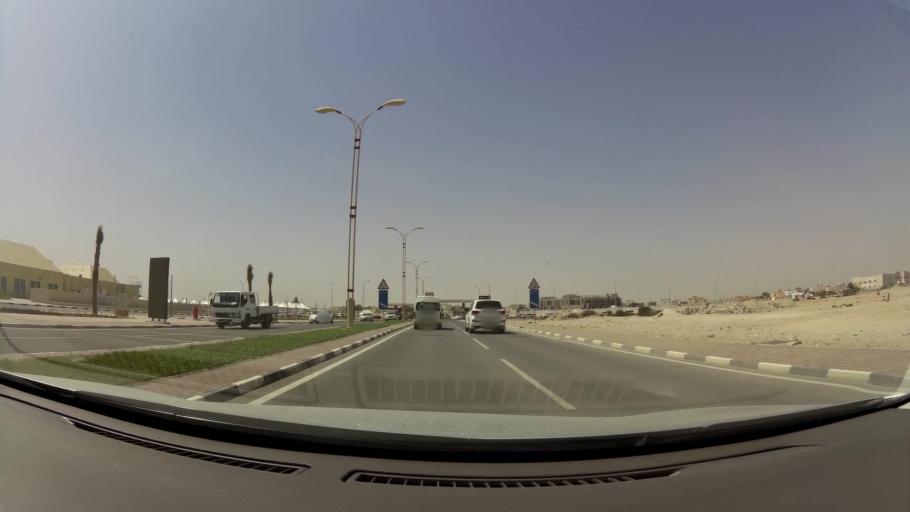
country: QA
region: Baladiyat Umm Salal
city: Umm Salal Muhammad
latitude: 25.3749
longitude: 51.4839
